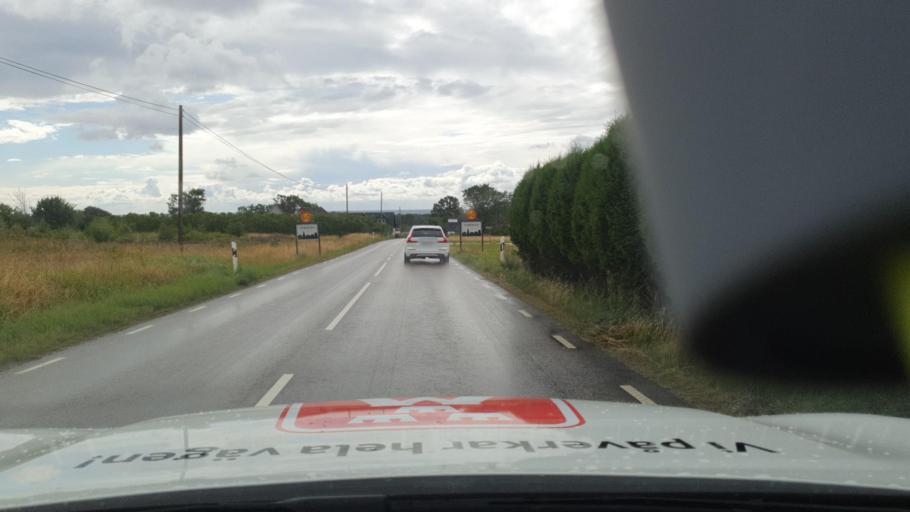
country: SE
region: Skane
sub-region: Angelholms Kommun
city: Vejbystrand
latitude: 56.4332
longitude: 12.6592
